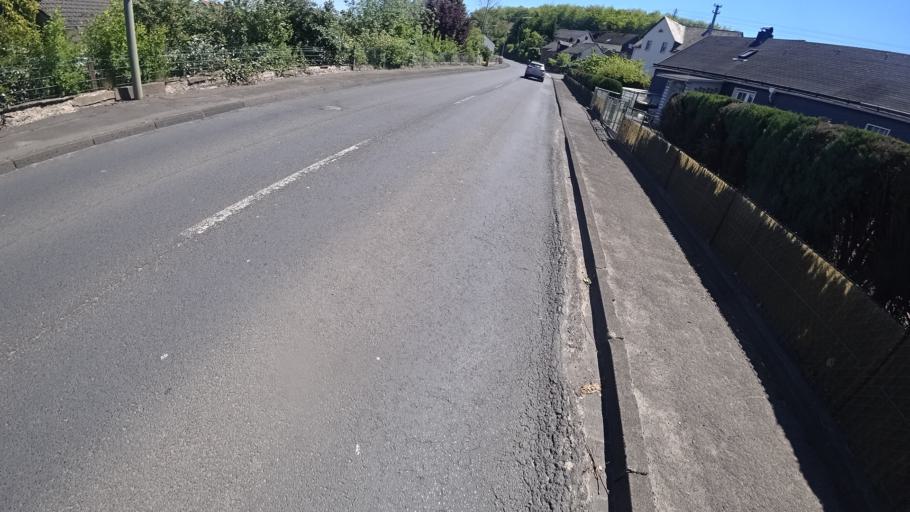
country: DE
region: Rheinland-Pfalz
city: Steineroth
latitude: 50.7596
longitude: 7.8537
